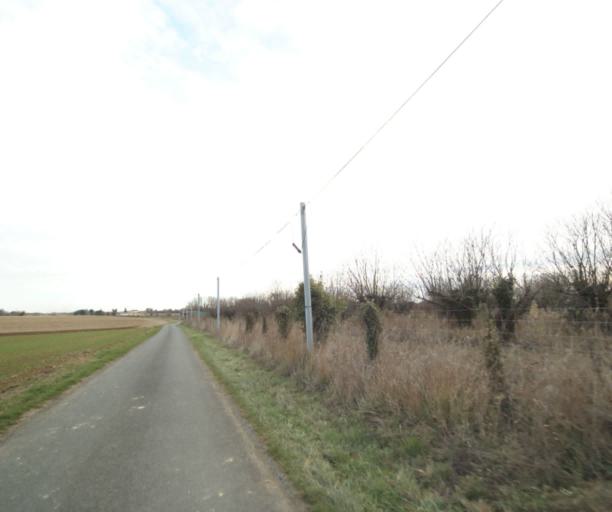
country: FR
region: Poitou-Charentes
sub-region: Departement de la Charente-Maritime
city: Corme-Royal
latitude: 45.7828
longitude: -0.8179
